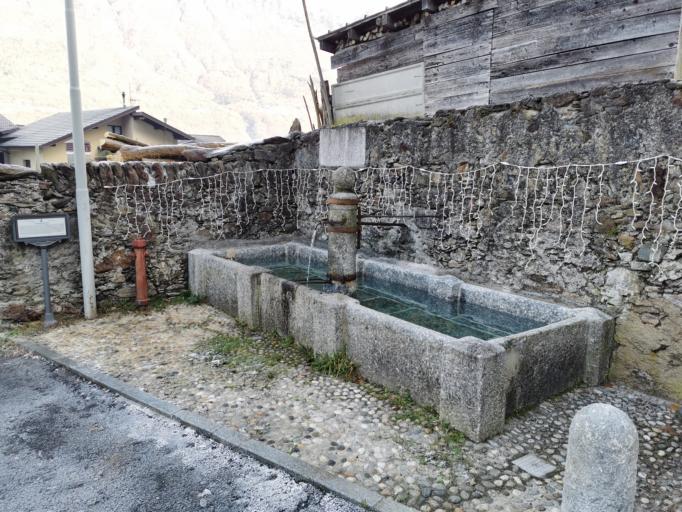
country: IT
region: Lombardy
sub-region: Provincia di Sondrio
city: Rogolo
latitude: 46.1345
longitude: 9.4883
